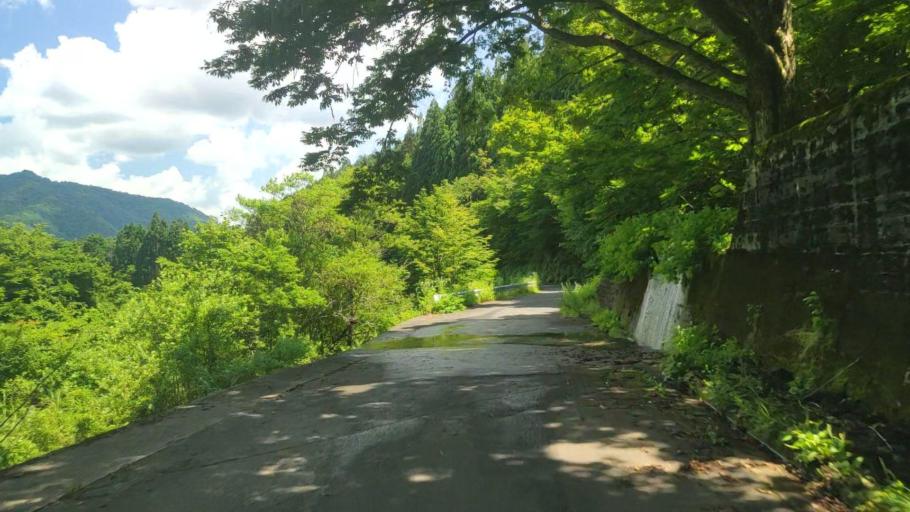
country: JP
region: Fukui
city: Ono
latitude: 35.7595
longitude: 136.5610
